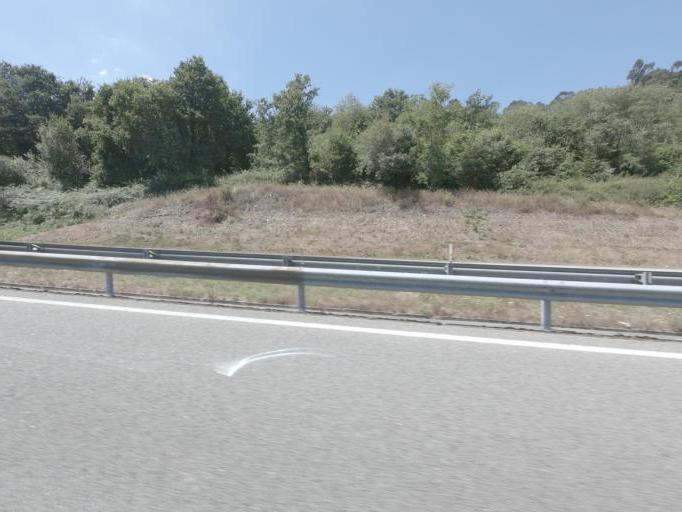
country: PT
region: Porto
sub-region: Marco de Canaveses
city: Marco de Canavezes
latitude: 41.2266
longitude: -8.1319
